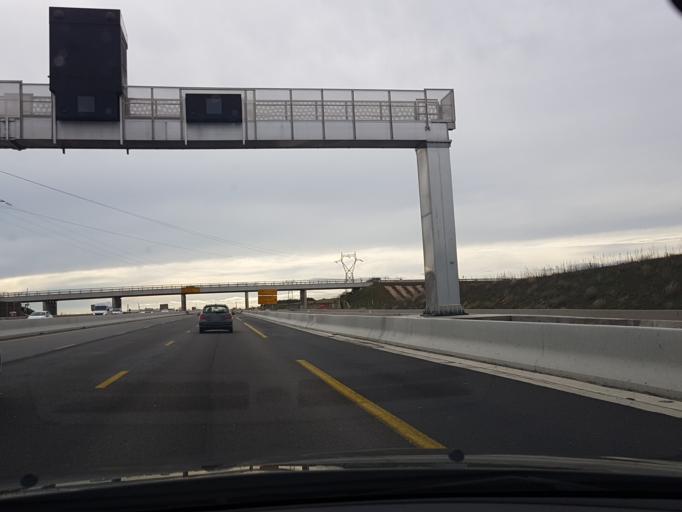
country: FR
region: Languedoc-Roussillon
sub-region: Departement de l'Herault
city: Baillargues
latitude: 43.6661
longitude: 4.0057
